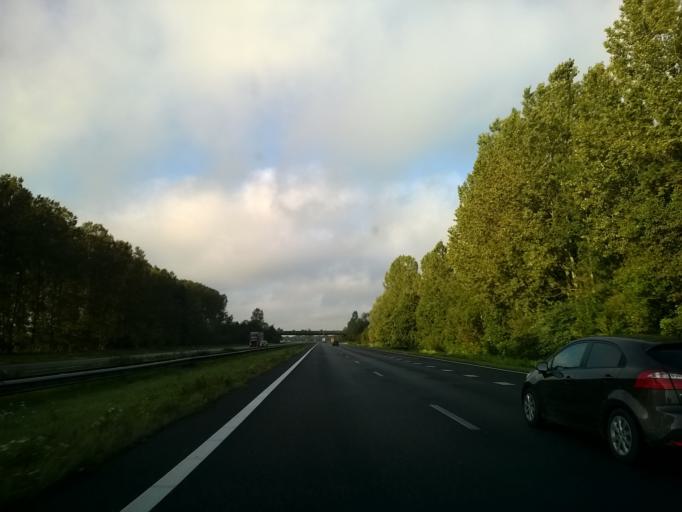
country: NL
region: Groningen
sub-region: Gemeente Grootegast
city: Grootegast
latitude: 53.1651
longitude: 6.3047
